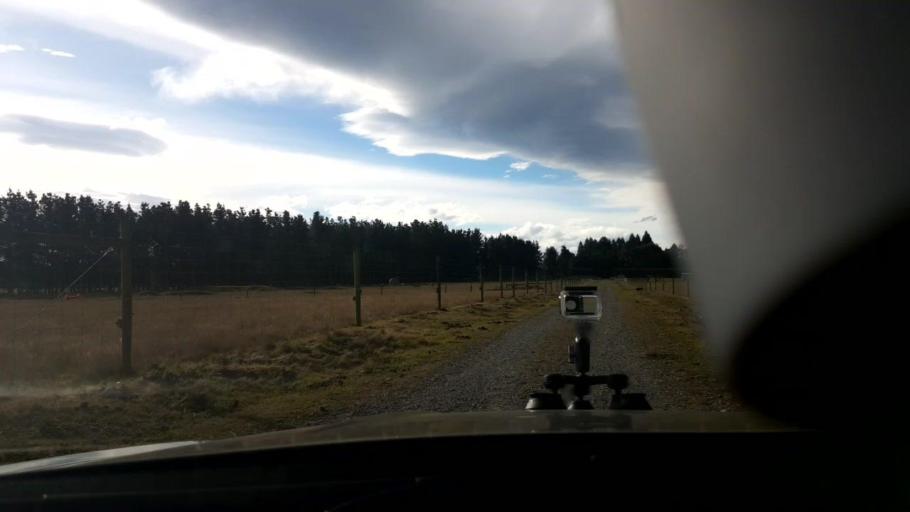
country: NZ
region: Canterbury
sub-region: Waimakariri District
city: Oxford
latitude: -43.4022
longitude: 172.3116
